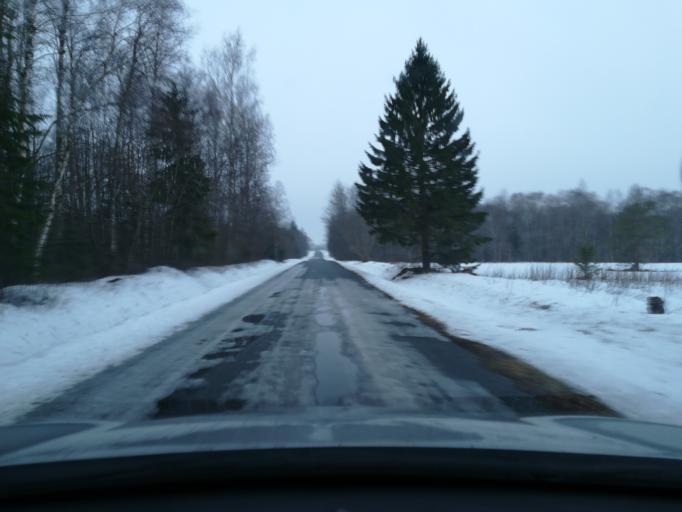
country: EE
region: Harju
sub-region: Raasiku vald
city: Raasiku
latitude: 59.3417
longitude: 25.2447
